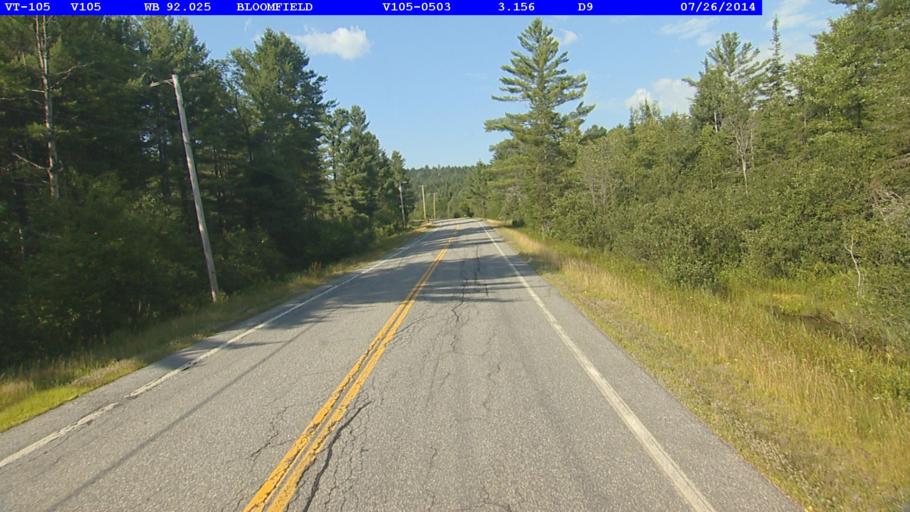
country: US
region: New Hampshire
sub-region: Coos County
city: Stratford
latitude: 44.7644
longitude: -71.6453
